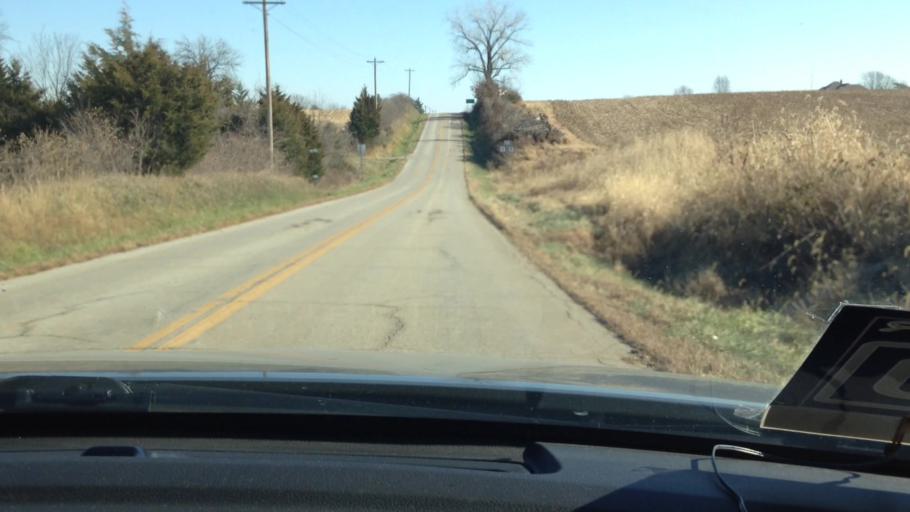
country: US
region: Missouri
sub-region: Platte County
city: Weston
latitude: 39.4977
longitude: -94.8496
